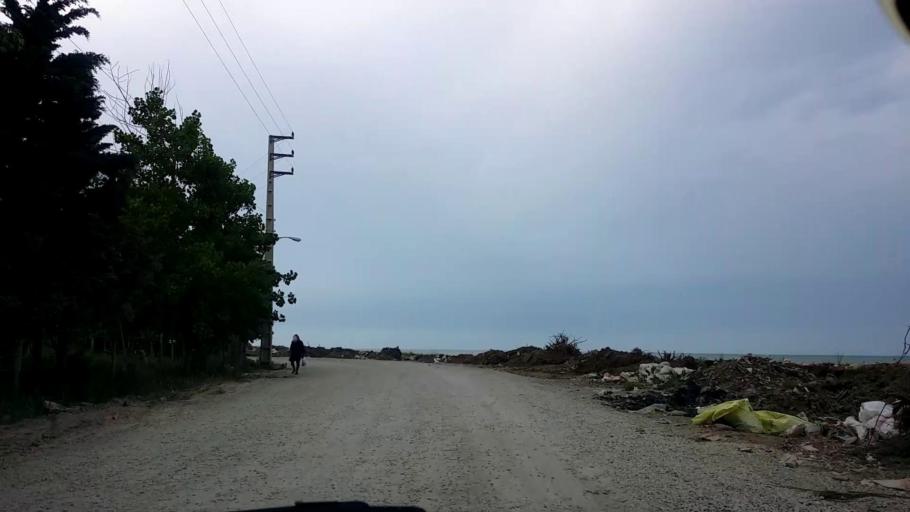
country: IR
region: Mazandaran
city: Chalus
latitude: 36.6832
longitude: 51.4334
